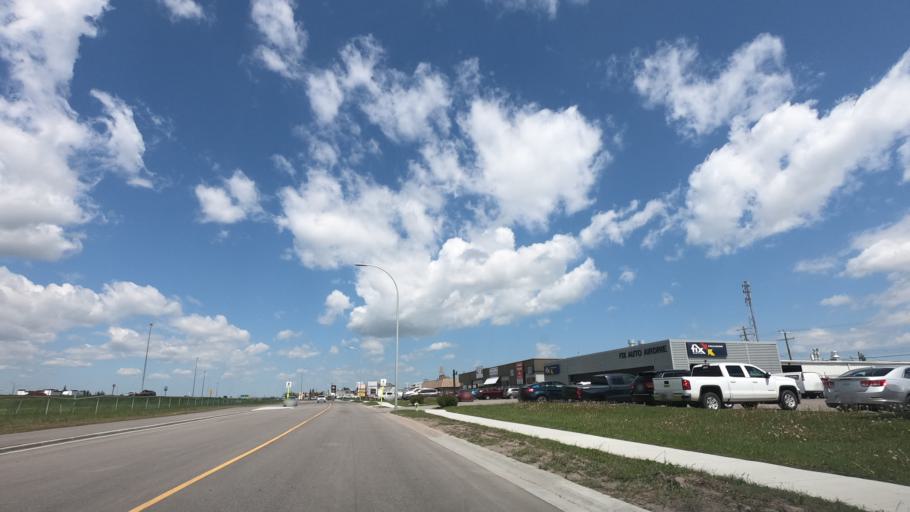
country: CA
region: Alberta
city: Airdrie
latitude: 51.2912
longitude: -113.9983
